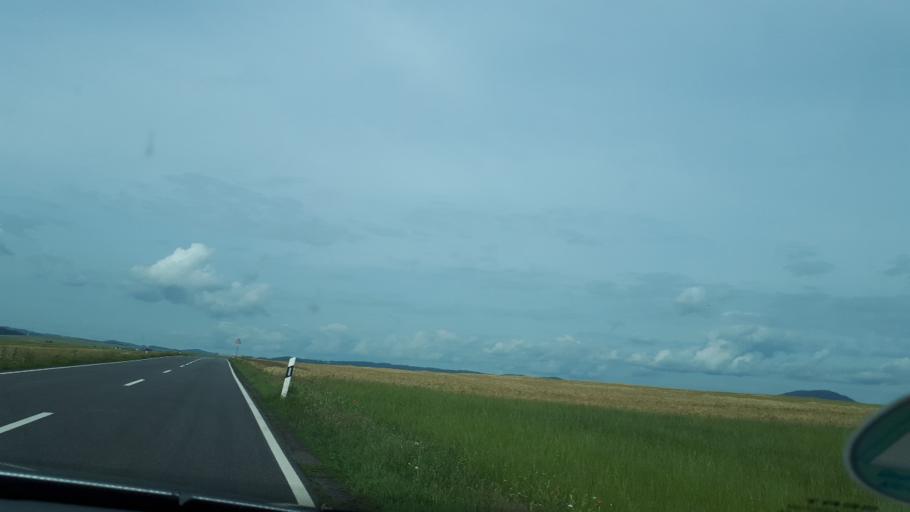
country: DE
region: Rheinland-Pfalz
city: Welling
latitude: 50.3337
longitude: 7.3001
